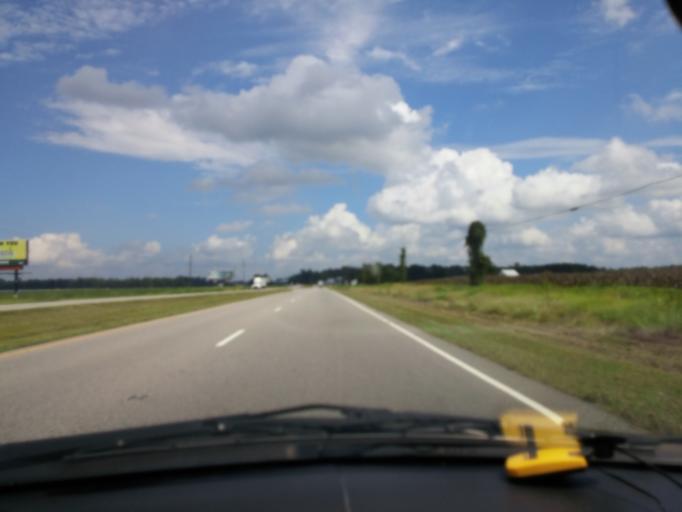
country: US
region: North Carolina
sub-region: Pitt County
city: Grifton
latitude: 35.3436
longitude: -77.4746
